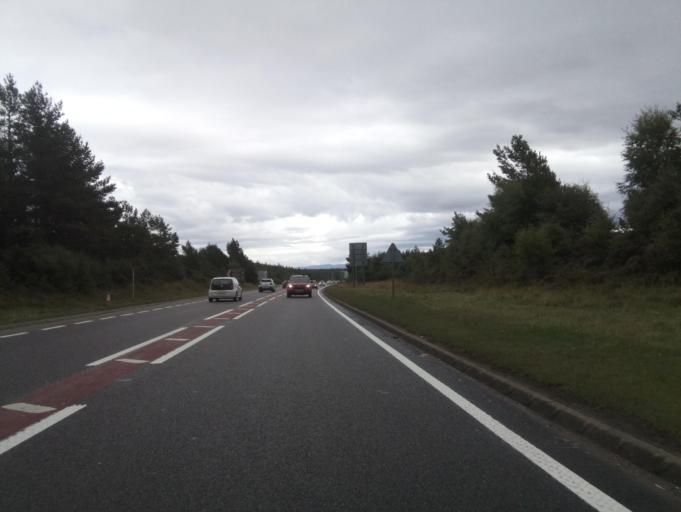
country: GB
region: Scotland
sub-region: Highland
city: Aviemore
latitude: 57.2930
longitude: -3.8666
